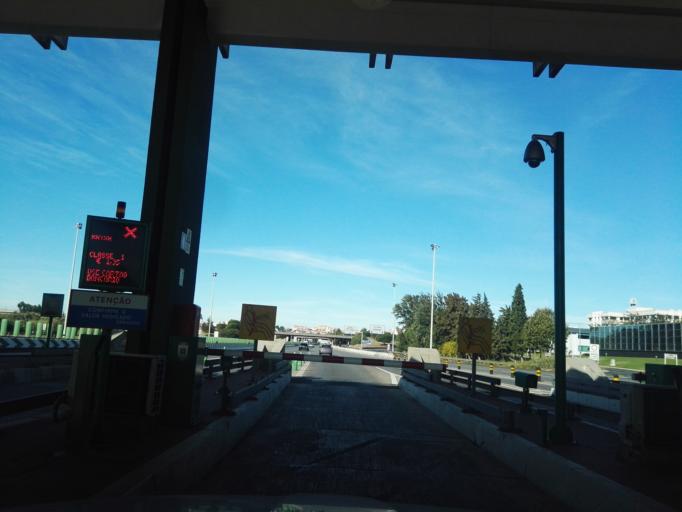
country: PT
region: Lisbon
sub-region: Cascais
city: Sao Domingos de Rana
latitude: 38.7081
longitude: -9.3345
